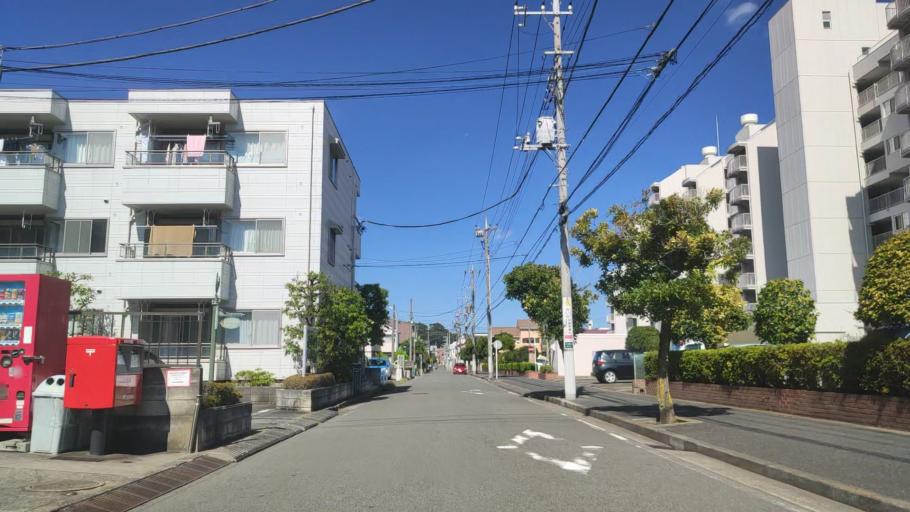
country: JP
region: Kanagawa
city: Yokohama
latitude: 35.5189
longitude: 139.6235
